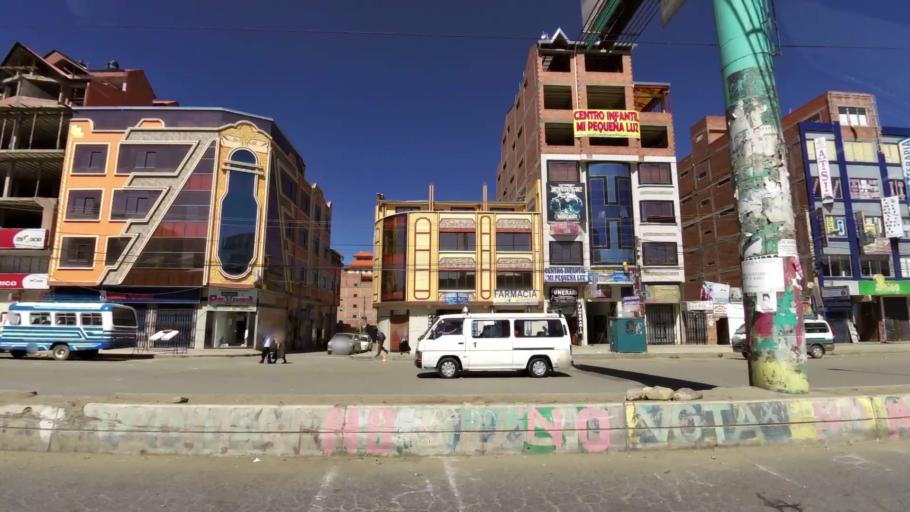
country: BO
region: La Paz
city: La Paz
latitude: -16.4901
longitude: -68.2067
